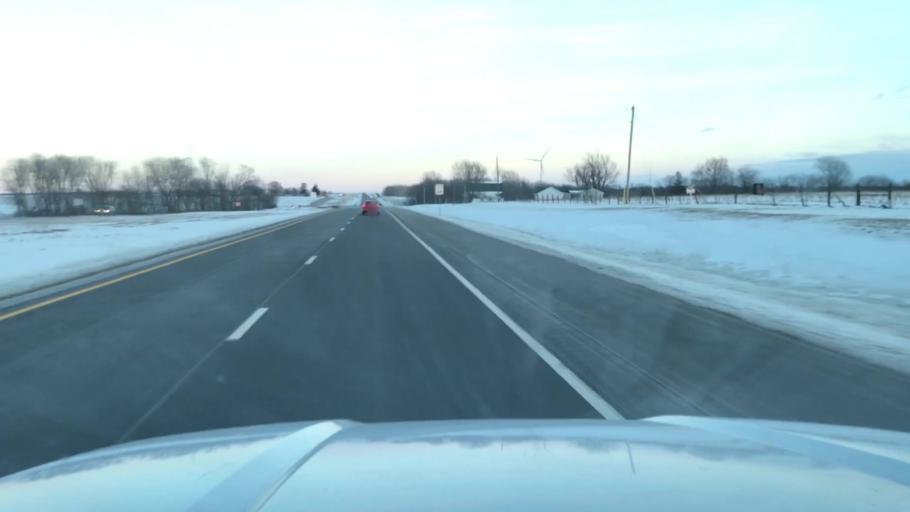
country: US
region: Missouri
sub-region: DeKalb County
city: Maysville
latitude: 39.7615
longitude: -94.4000
